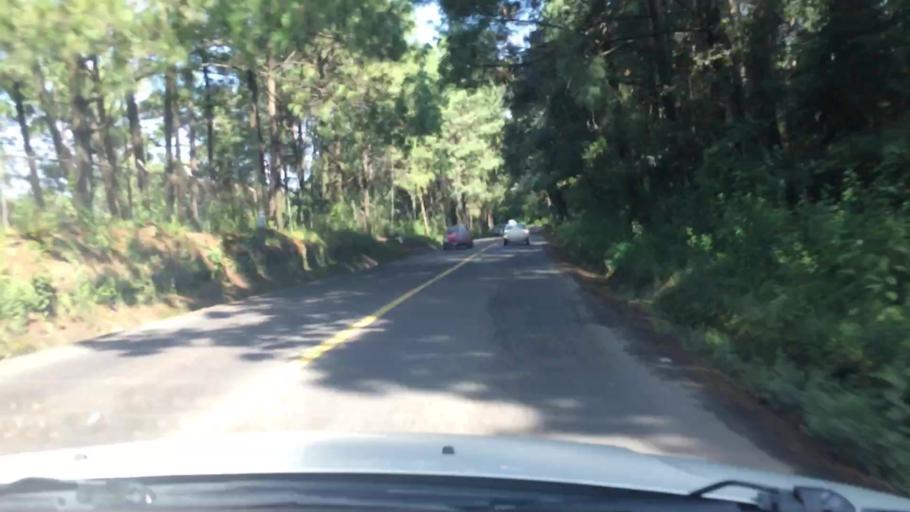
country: MX
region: Mexico
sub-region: Valle de Bravo
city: Casas Viejas
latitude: 19.1558
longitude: -100.0931
